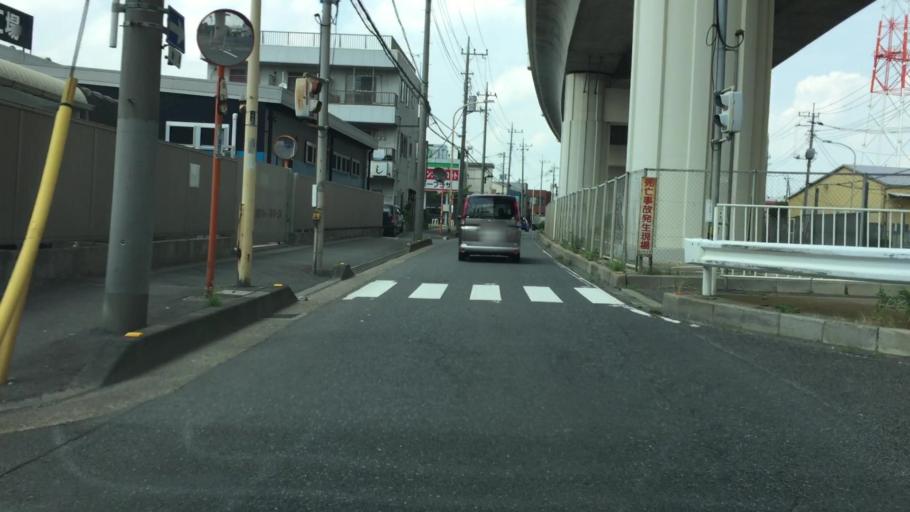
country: JP
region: Saitama
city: Yashio-shi
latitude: 35.7966
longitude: 139.8272
